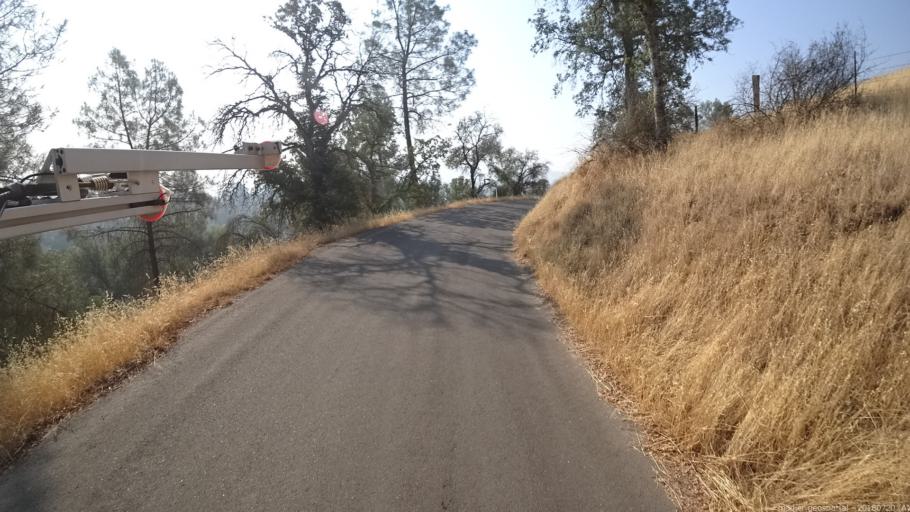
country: US
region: California
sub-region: Madera County
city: Yosemite Lakes
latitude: 37.3050
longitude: -119.8687
